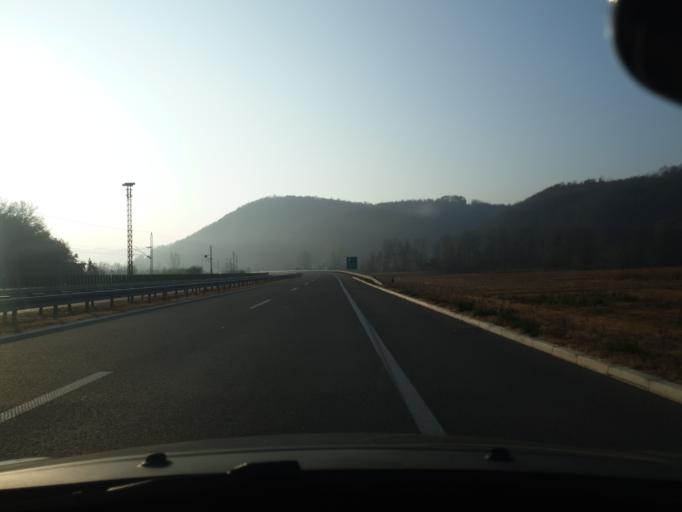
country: RS
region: Central Serbia
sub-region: Jablanicki Okrug
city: Vlasotince
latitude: 42.9000
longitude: 22.0510
